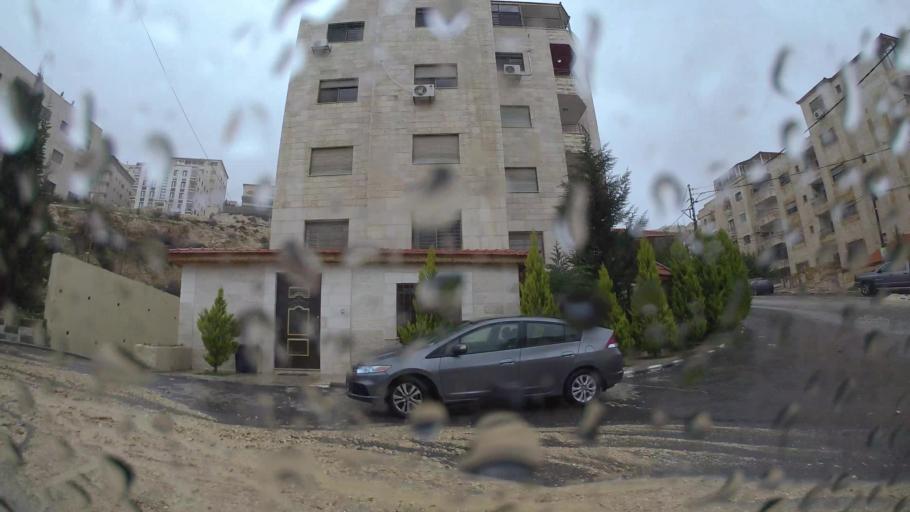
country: JO
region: Amman
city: Al Jubayhah
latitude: 32.0198
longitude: 35.8935
